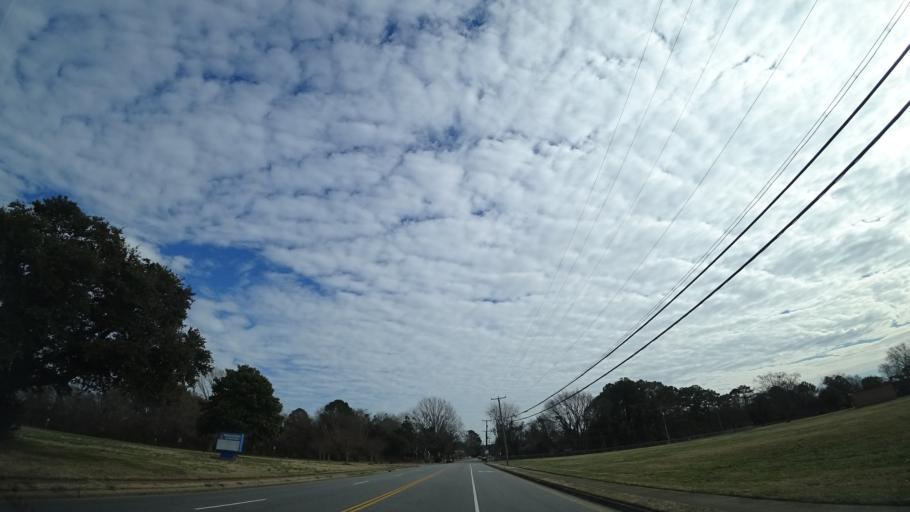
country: US
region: Virginia
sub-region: City of Hampton
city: Hampton
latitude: 37.0509
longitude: -76.3852
